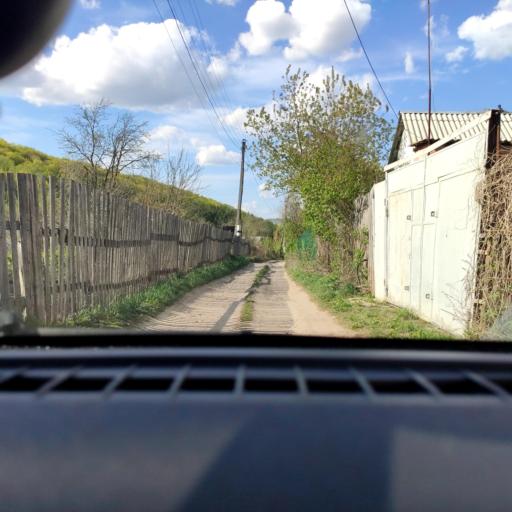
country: RU
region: Samara
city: Zhigulevsk
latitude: 53.3726
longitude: 49.5092
